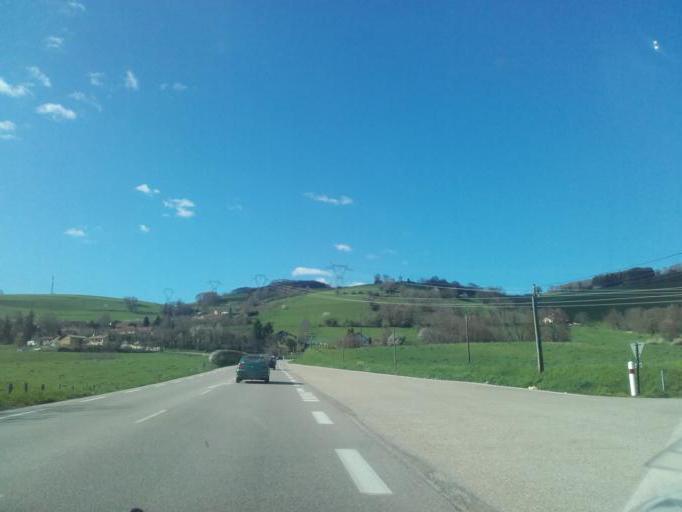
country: FR
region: Rhone-Alpes
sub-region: Departement de l'Isere
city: Saint-Hilaire-de-la-Cote
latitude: 45.3967
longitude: 5.3584
